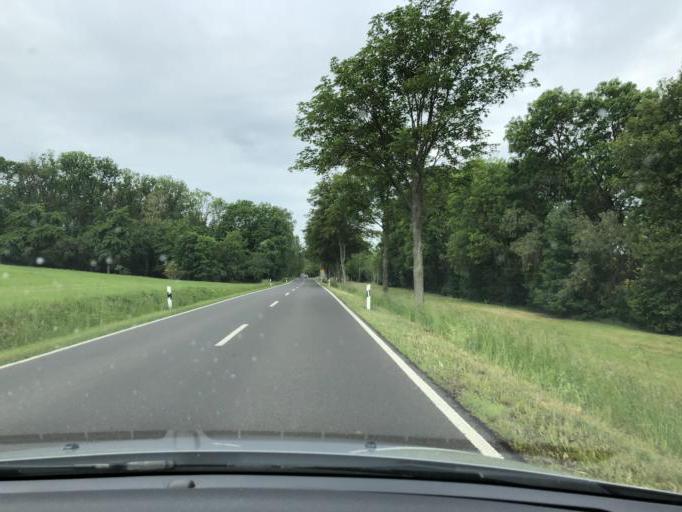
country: DE
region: Thuringia
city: Nirmsdorf
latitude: 51.0945
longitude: 11.4770
